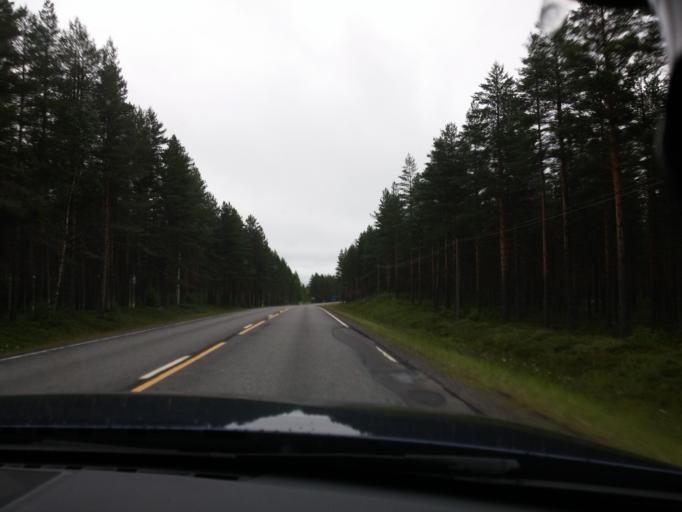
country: FI
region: Pirkanmaa
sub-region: Ylae-Pirkanmaa
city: Vilppula
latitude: 61.9437
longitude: 24.5418
